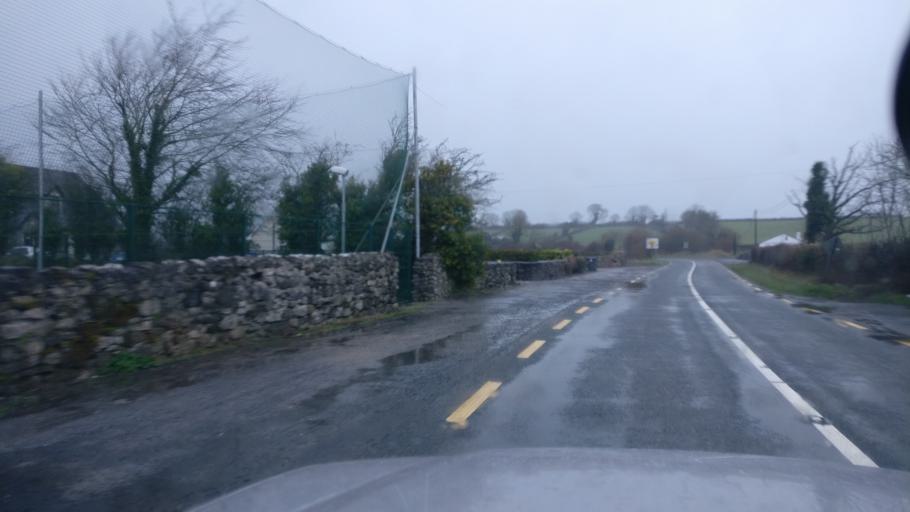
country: IE
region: Connaught
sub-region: County Galway
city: Loughrea
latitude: 53.1599
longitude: -8.4863
